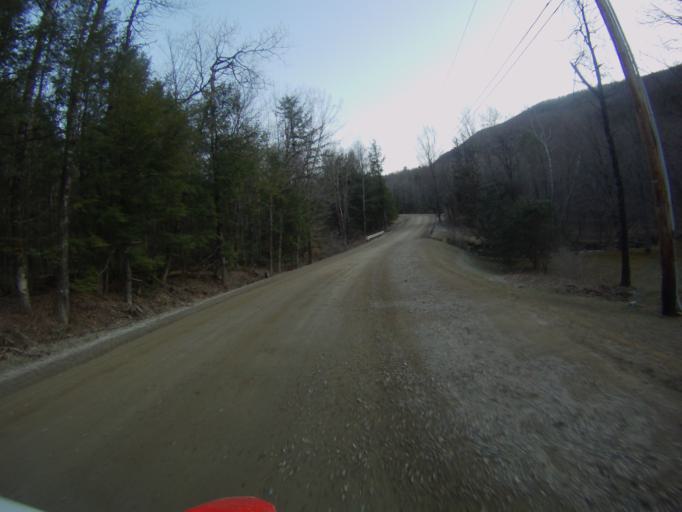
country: US
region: Vermont
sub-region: Addison County
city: Bristol
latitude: 44.0746
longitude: -73.0602
